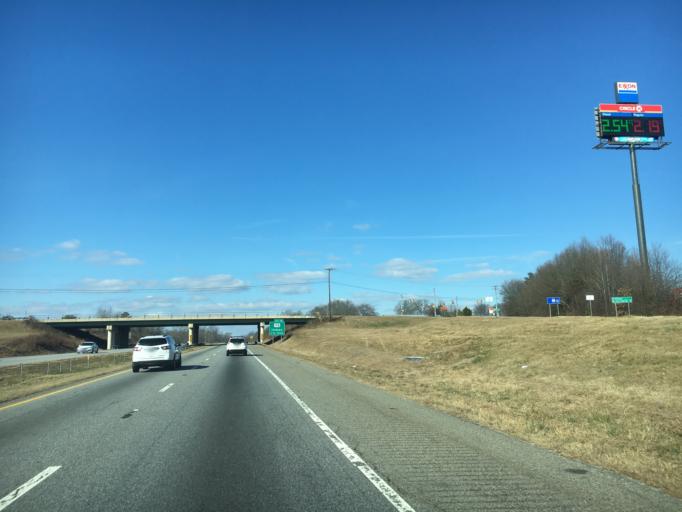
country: US
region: South Carolina
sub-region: Spartanburg County
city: Southern Shops
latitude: 35.0082
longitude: -82.0270
